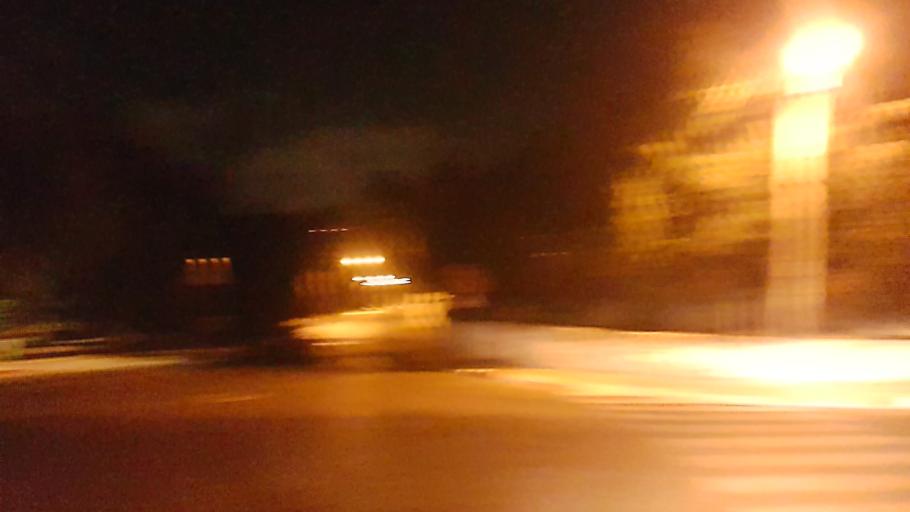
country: IL
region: Central District
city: Hod HaSharon
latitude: 32.1675
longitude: 34.8898
